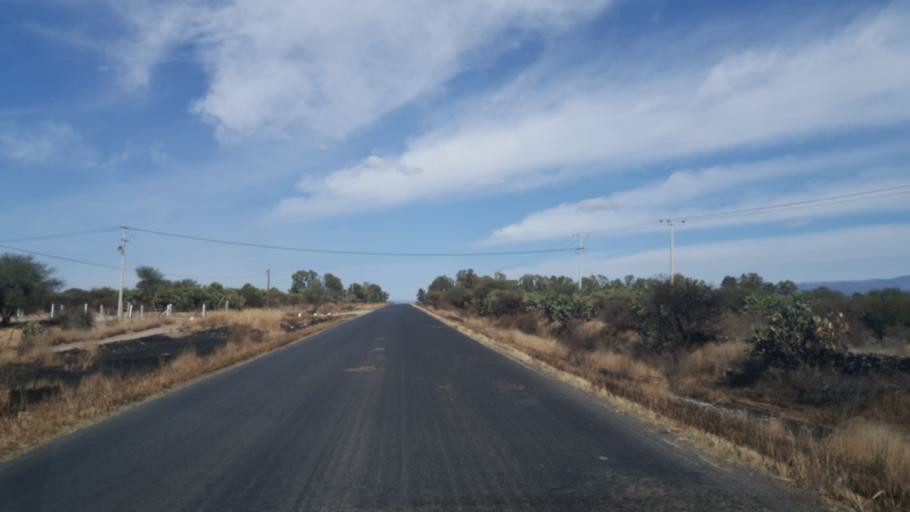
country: MX
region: Jalisco
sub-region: Lagos de Moreno
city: Geovillas Laureles del Campanario
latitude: 21.2857
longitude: -101.9341
